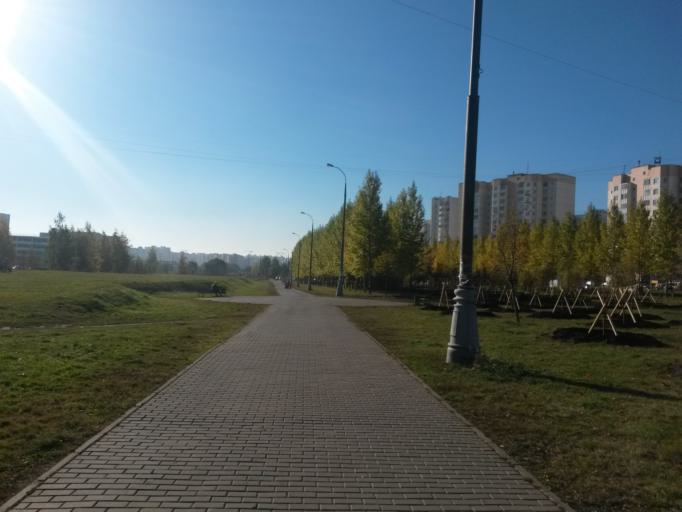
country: RU
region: Moskovskaya
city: Kommunarka
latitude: 55.5441
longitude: 37.5142
